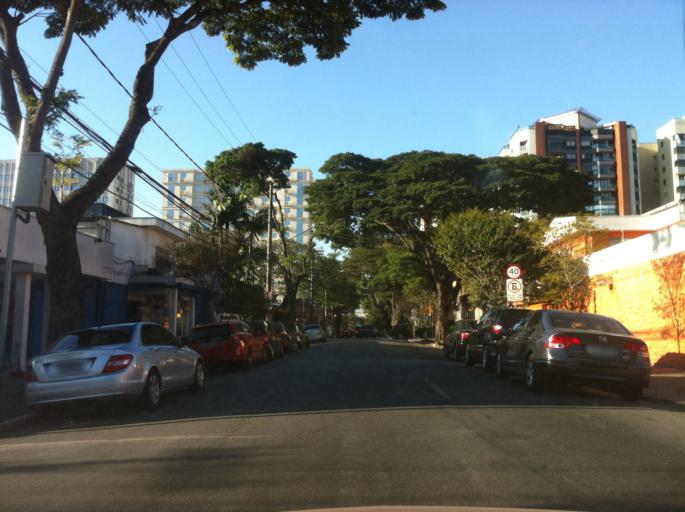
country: BR
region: Sao Paulo
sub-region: Sao Paulo
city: Sao Paulo
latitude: -23.6140
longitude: -46.6659
